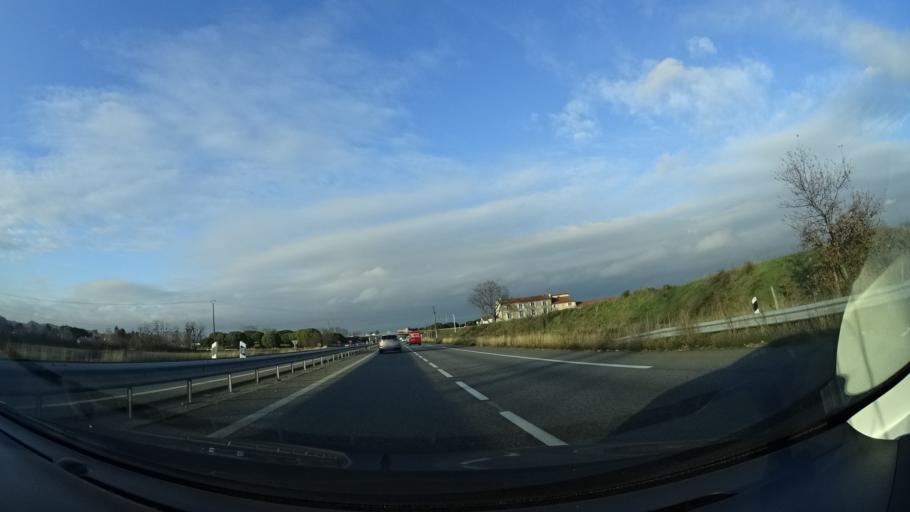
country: FR
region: Midi-Pyrenees
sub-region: Departement de l'Ariege
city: Saint-Jean-du-Falga
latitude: 43.0989
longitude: 1.6331
